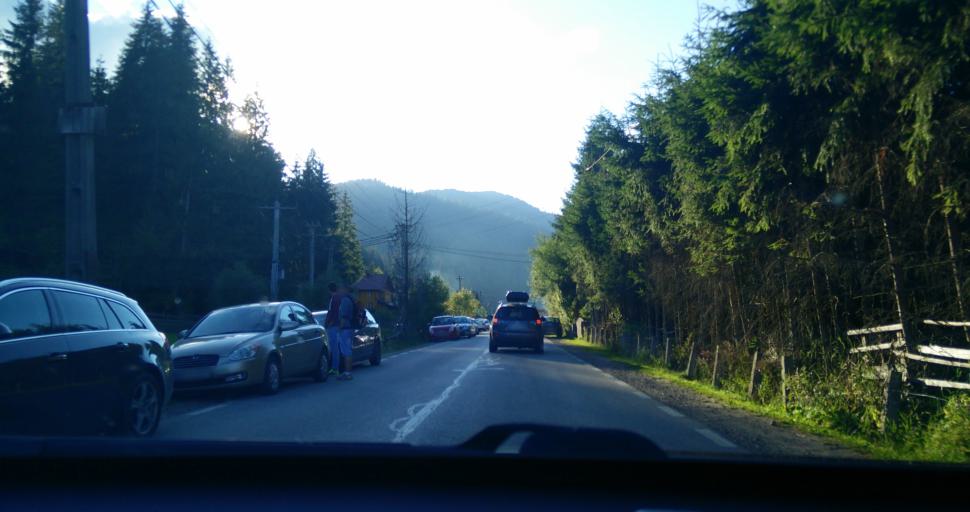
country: RO
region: Alba
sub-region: Comuna Arieseni
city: Arieseni
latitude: 46.4815
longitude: 22.7263
